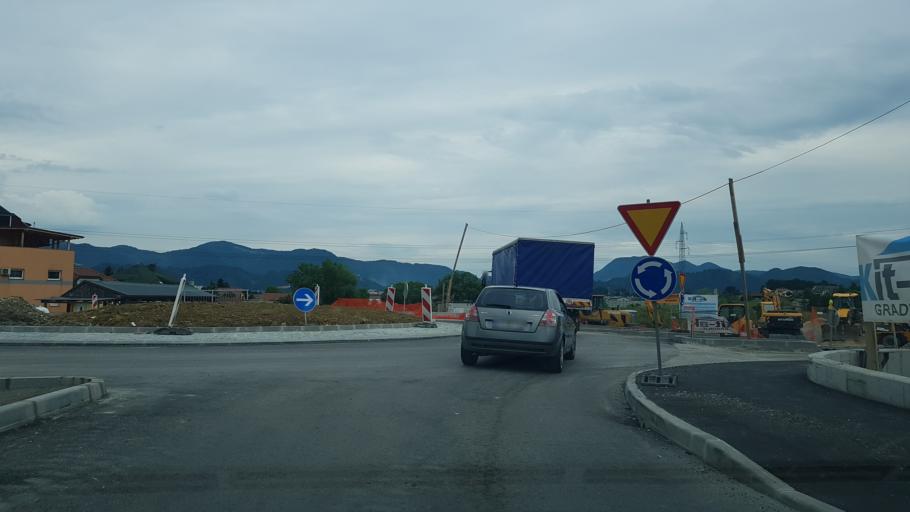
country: SI
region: Celje
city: Trnovlje pri Celju
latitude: 46.2599
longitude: 15.2818
